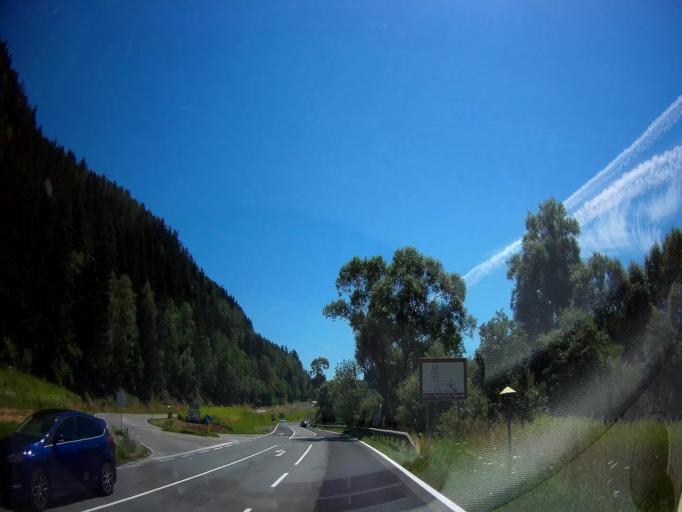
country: AT
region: Carinthia
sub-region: Politischer Bezirk Sankt Veit an der Glan
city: Micheldorf
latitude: 46.9003
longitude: 14.4405
